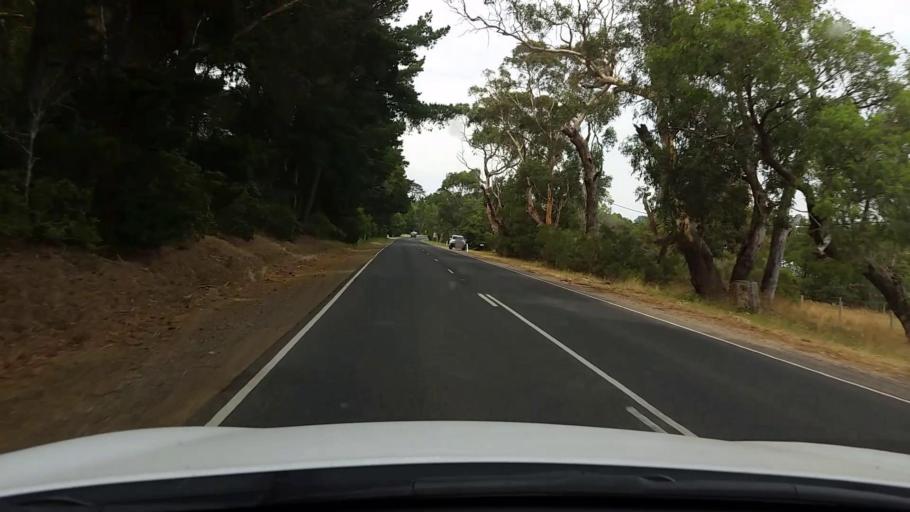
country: AU
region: Victoria
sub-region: Mornington Peninsula
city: Merricks
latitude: -38.3948
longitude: 145.0843
